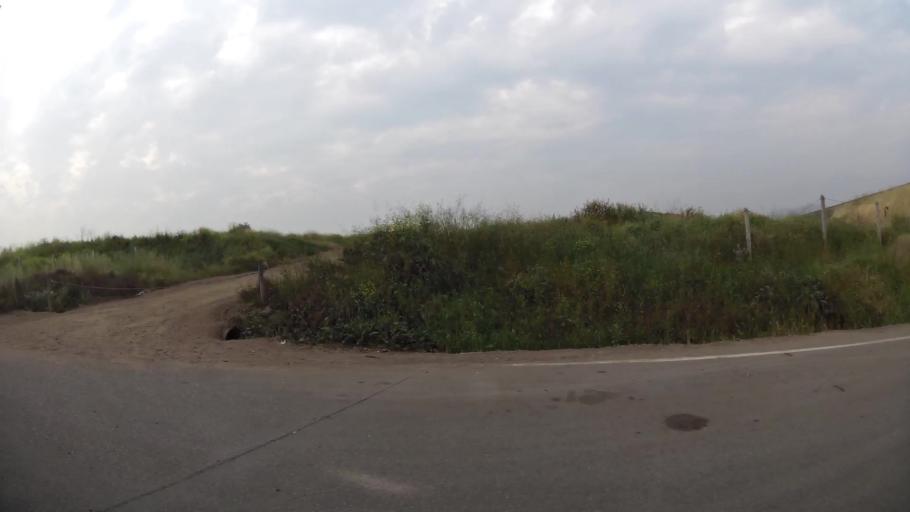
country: CL
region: Santiago Metropolitan
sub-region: Provincia de Chacabuco
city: Chicureo Abajo
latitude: -33.2073
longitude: -70.6680
